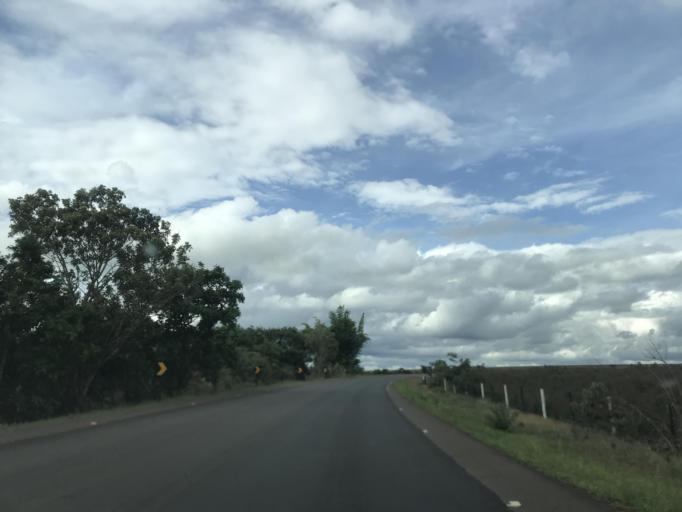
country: BR
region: Goias
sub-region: Vianopolis
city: Vianopolis
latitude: -16.9821
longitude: -48.6680
